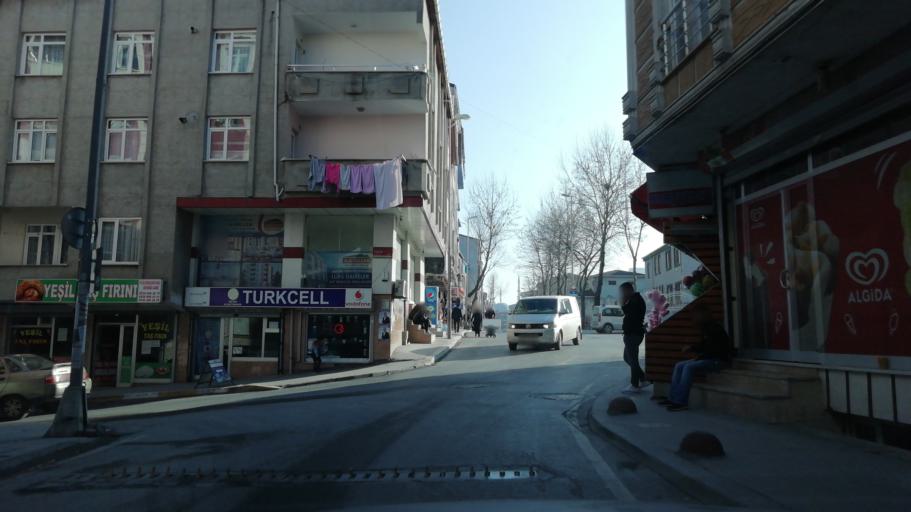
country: TR
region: Istanbul
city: Esenyurt
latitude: 41.0309
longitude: 28.6894
